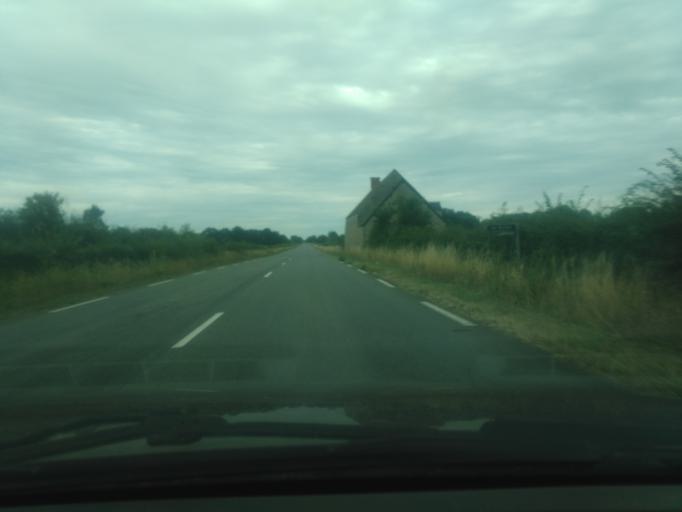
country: FR
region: Centre
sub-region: Departement du Cher
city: Charenton-du-Cher
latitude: 46.7311
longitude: 2.6036
